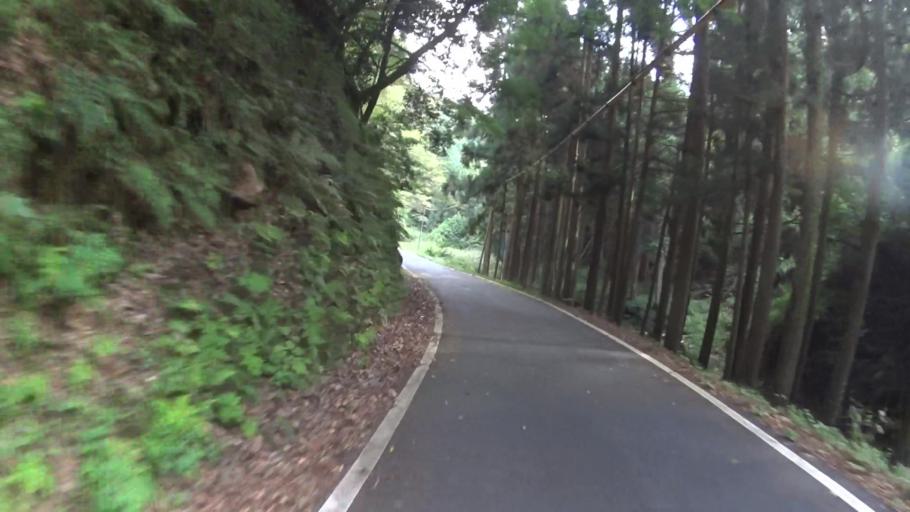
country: JP
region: Kyoto
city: Miyazu
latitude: 35.6102
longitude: 135.2068
